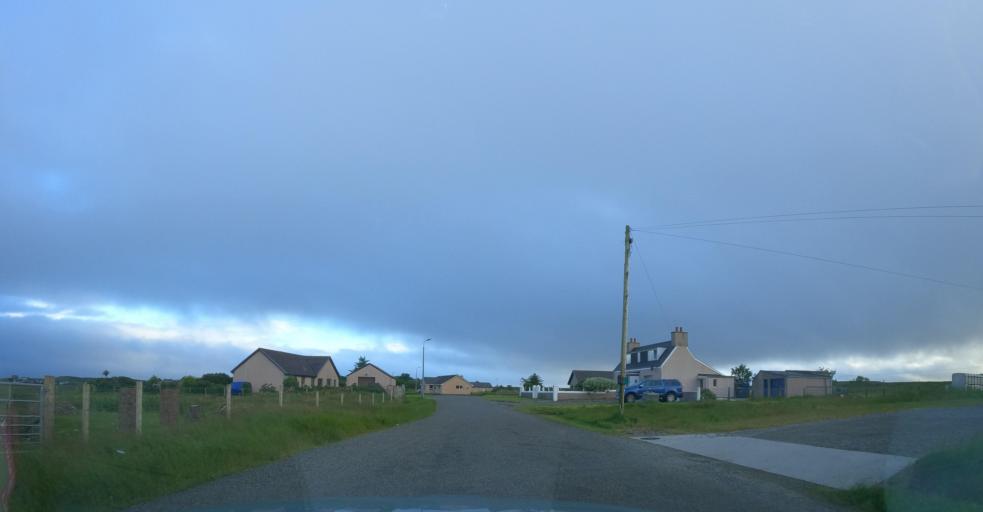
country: GB
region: Scotland
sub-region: Eilean Siar
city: Stornoway
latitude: 58.1996
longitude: -6.2246
